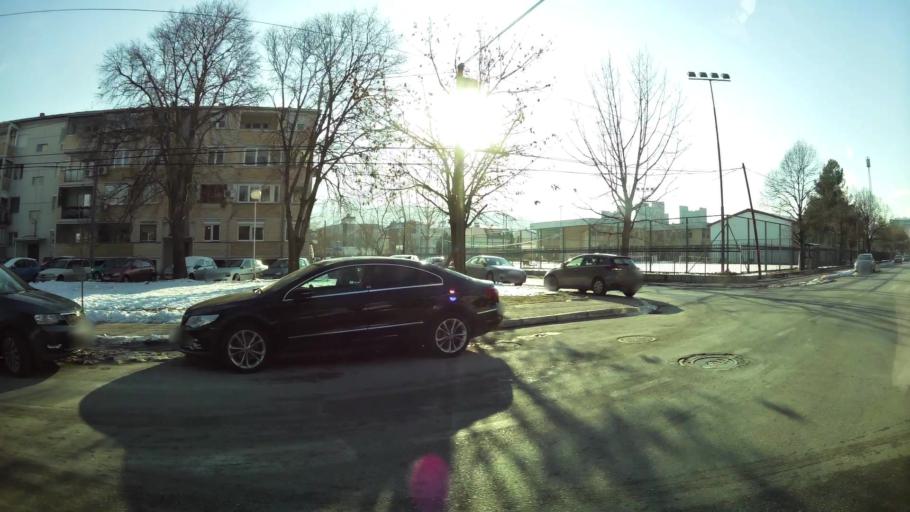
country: MK
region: Karpos
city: Skopje
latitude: 42.0012
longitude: 21.3951
